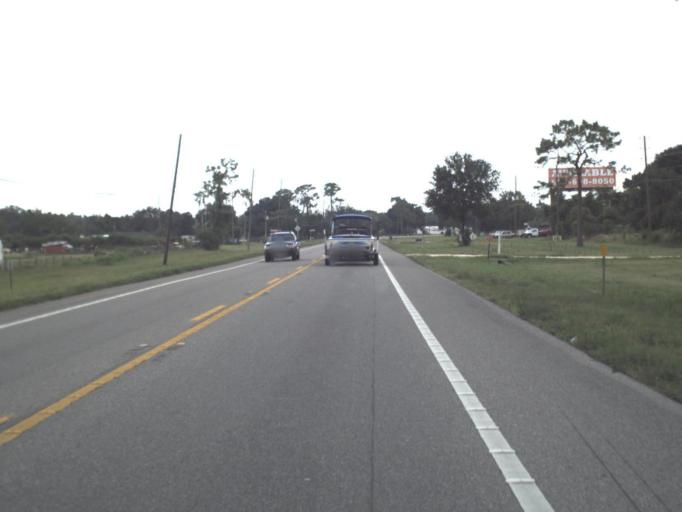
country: US
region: Florida
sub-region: Pasco County
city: Land O' Lakes
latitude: 28.3086
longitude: -82.5027
